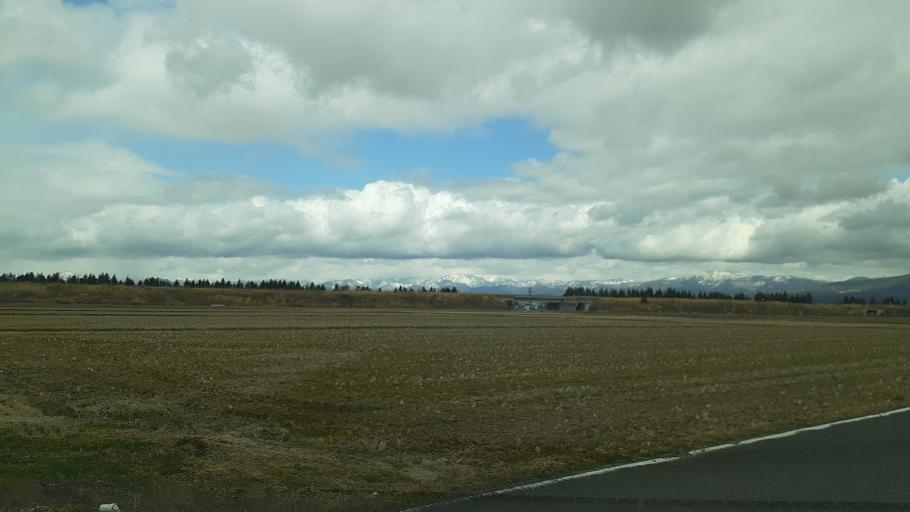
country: JP
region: Fukushima
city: Kitakata
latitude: 37.5313
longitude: 139.8867
